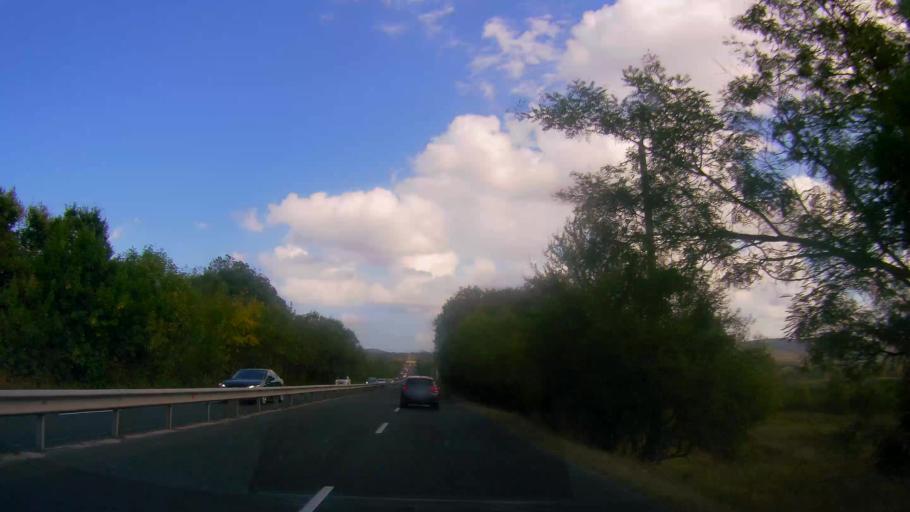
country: BG
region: Burgas
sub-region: Obshtina Burgas
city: Burgas
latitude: 42.4287
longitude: 27.5056
